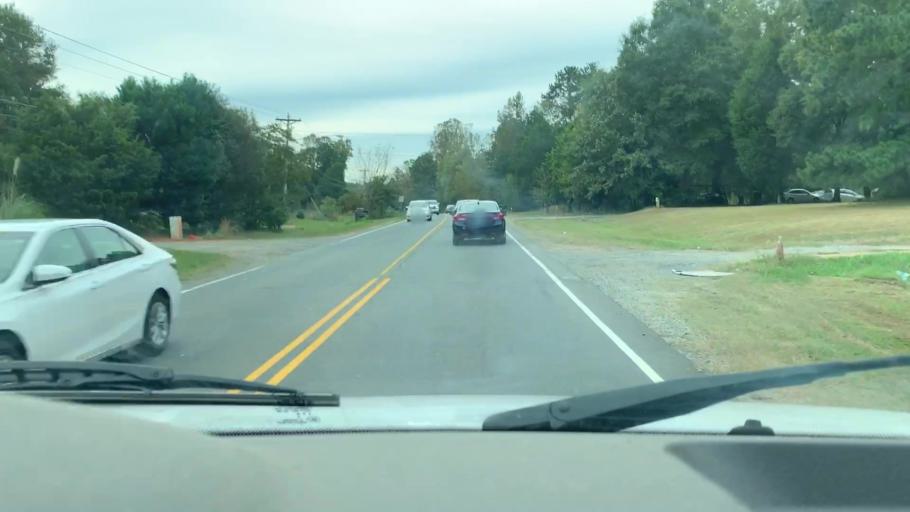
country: US
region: North Carolina
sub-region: Mecklenburg County
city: Huntersville
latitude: 35.4345
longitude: -80.8650
